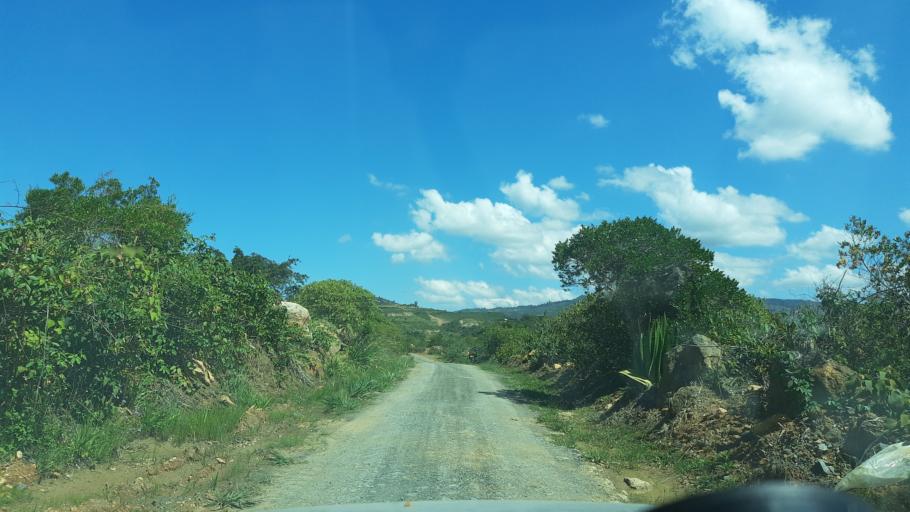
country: CO
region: Boyaca
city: Santa Sofia
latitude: 5.6924
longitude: -73.5834
